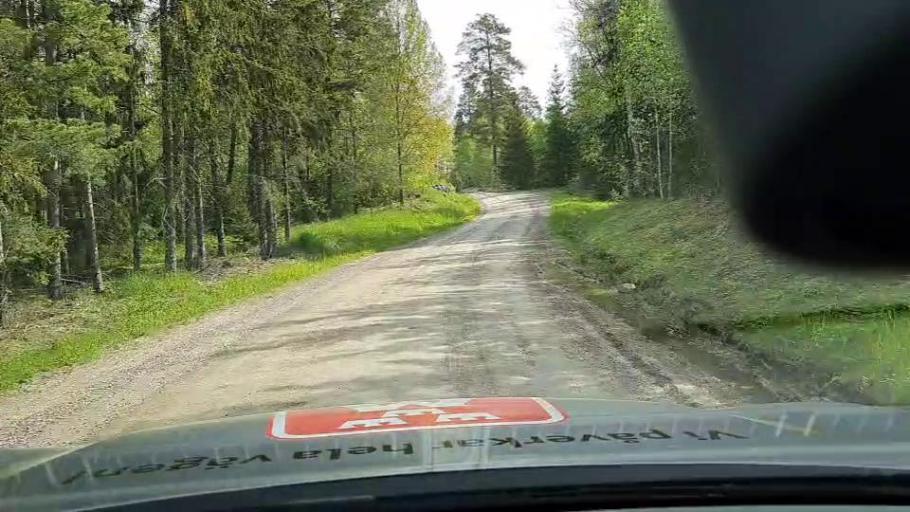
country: SE
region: Soedermanland
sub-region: Strangnas Kommun
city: Strangnas
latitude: 59.2620
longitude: 16.8772
